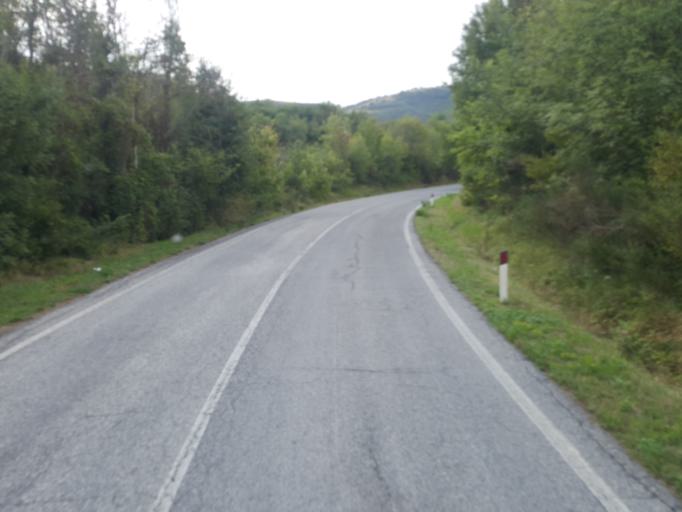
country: IT
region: Umbria
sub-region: Provincia di Perugia
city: Fossato di Vico
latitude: 43.3276
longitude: 12.8314
